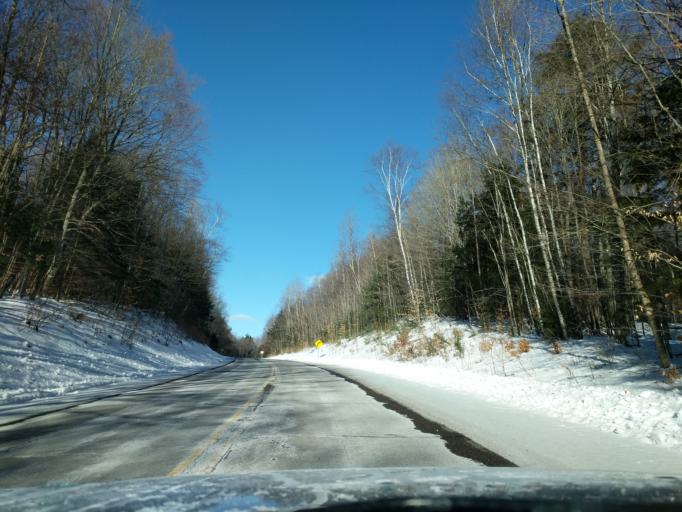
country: US
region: Wisconsin
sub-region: Menominee County
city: Keshena
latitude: 45.0971
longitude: -88.6339
